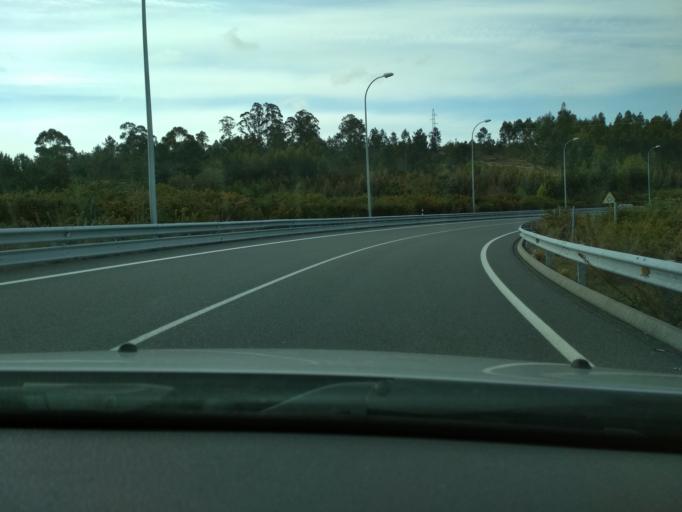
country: ES
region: Galicia
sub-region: Provincia da Coruna
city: Culleredo
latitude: 43.2922
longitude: -8.4039
